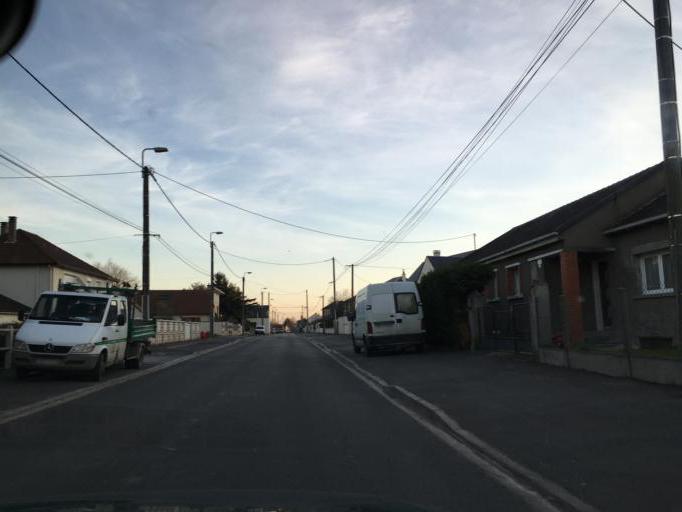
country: FR
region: Centre
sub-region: Departement du Loiret
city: Saran
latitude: 47.9453
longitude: 1.8717
